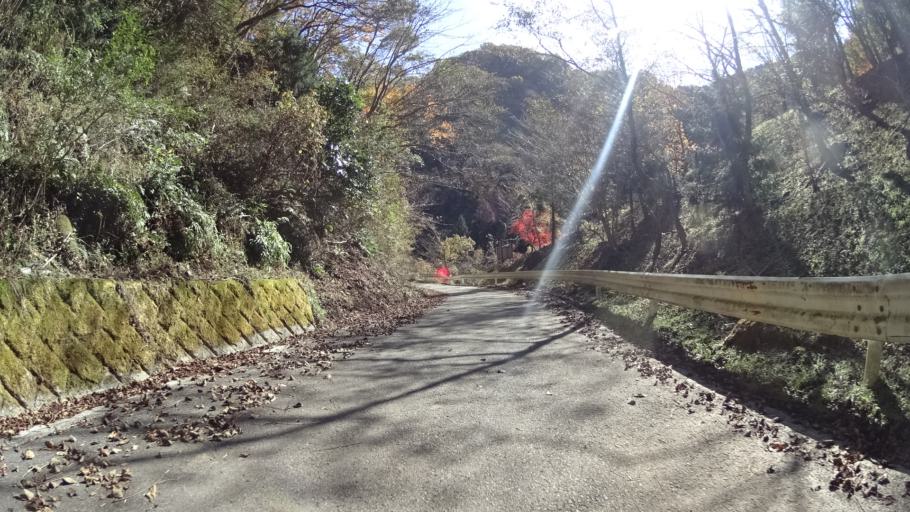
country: JP
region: Kanagawa
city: Atsugi
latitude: 35.5106
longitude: 139.2688
